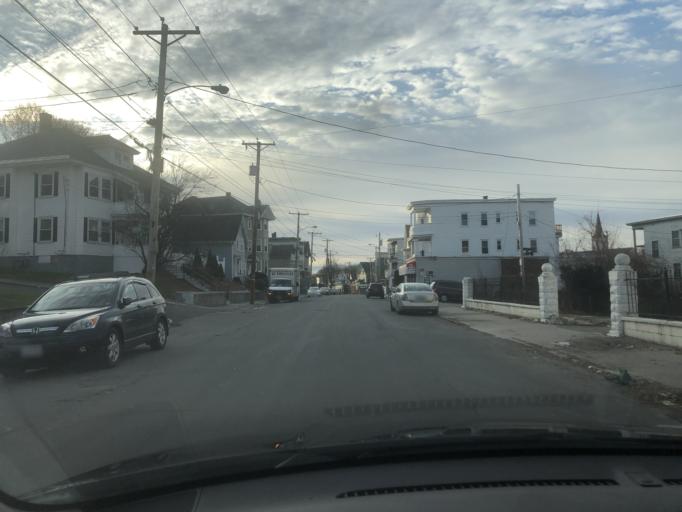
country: US
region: Massachusetts
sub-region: Essex County
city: Lawrence
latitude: 42.7187
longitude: -71.1551
